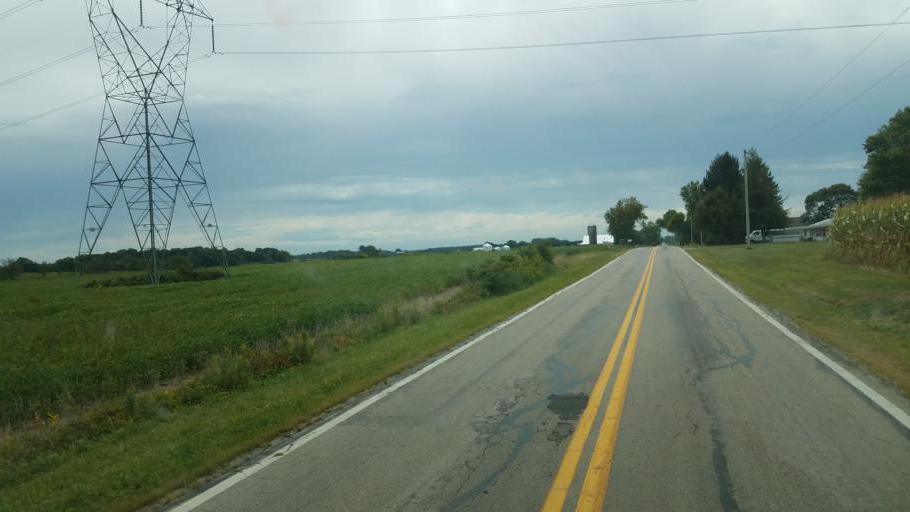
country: US
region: Ohio
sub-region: Knox County
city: Centerburg
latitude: 40.2713
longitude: -82.7512
